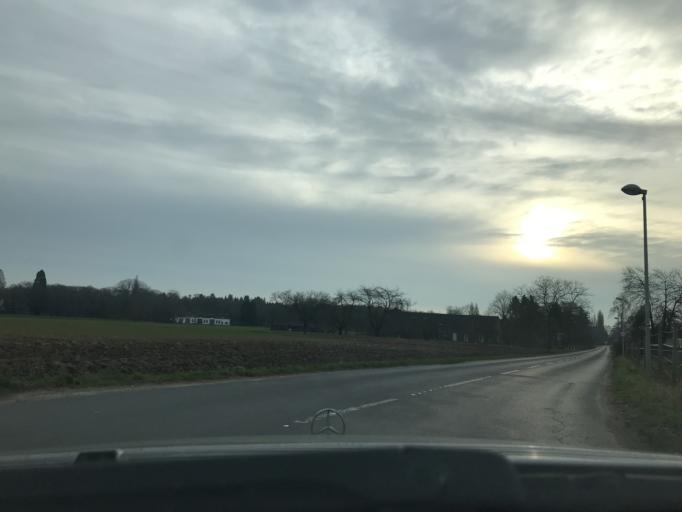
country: DE
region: North Rhine-Westphalia
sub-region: Regierungsbezirk Dusseldorf
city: Krefeld
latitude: 51.3887
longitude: 6.5524
